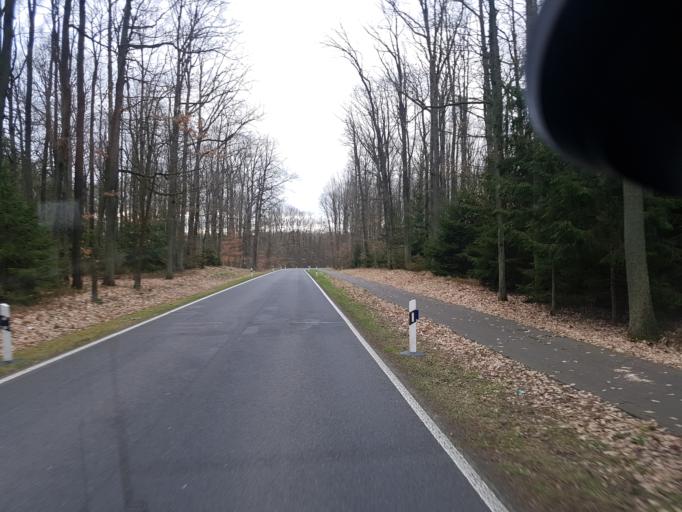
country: DE
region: Brandenburg
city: Gross Lindow
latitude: 52.1708
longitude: 14.4923
